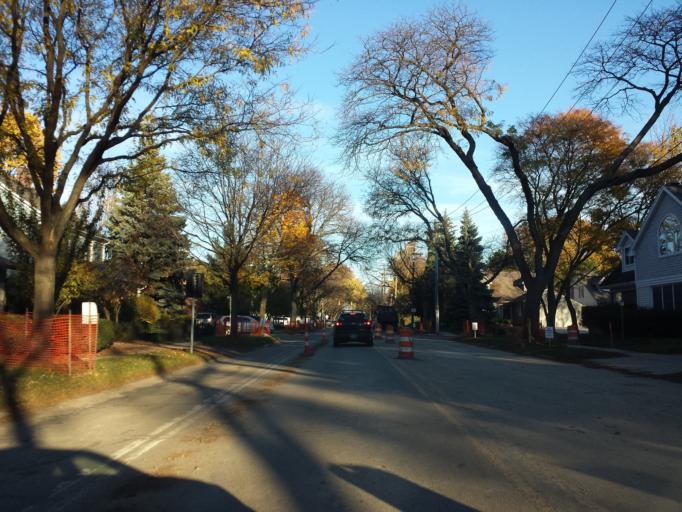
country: US
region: Michigan
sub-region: Oakland County
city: Birmingham
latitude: 42.5389
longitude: -83.2164
